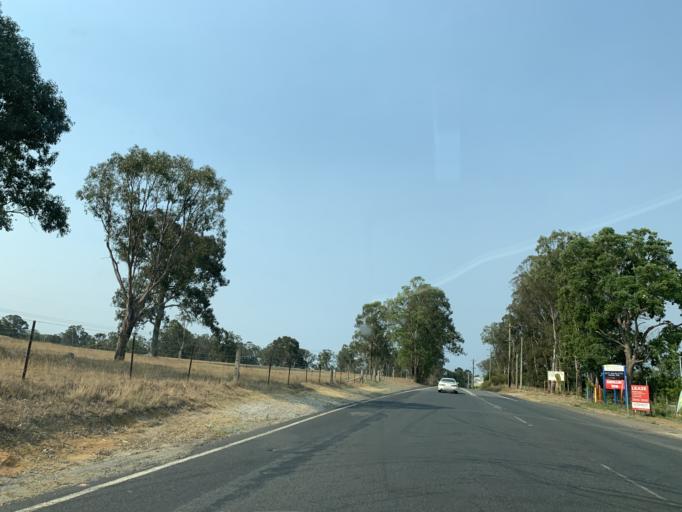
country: AU
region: New South Wales
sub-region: Blacktown
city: Rouse Hill
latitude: -33.6653
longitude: 150.9188
